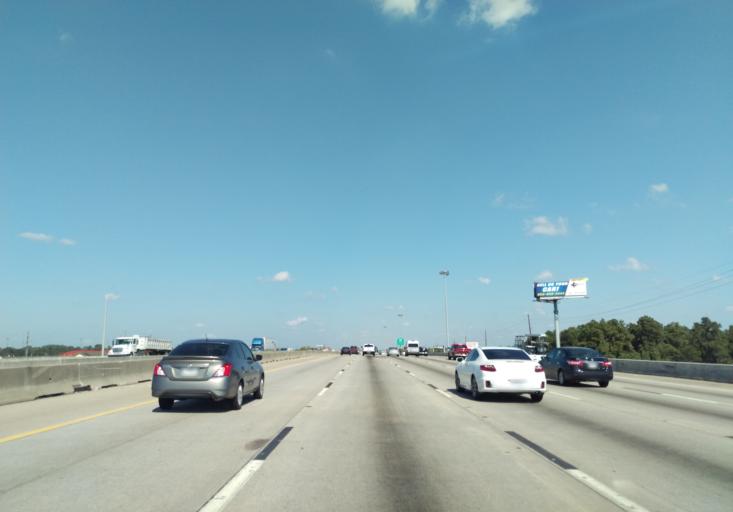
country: US
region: Texas
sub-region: Harris County
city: Aldine
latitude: 29.9966
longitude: -95.4253
